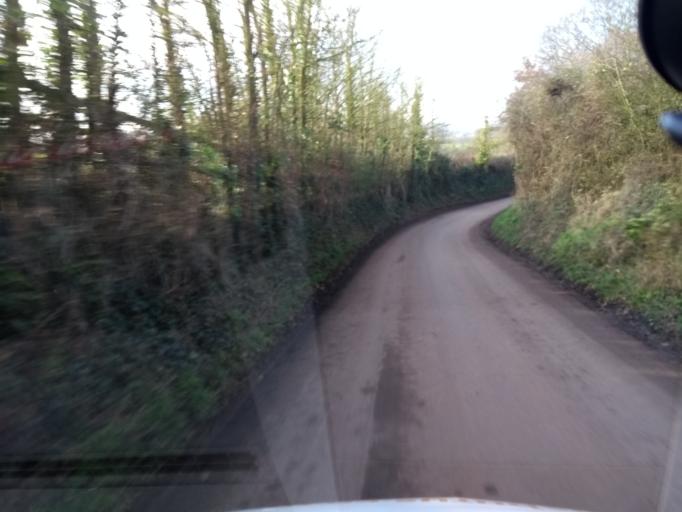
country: GB
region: England
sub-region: Somerset
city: Creech Saint Michael
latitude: 51.0228
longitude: -3.0005
